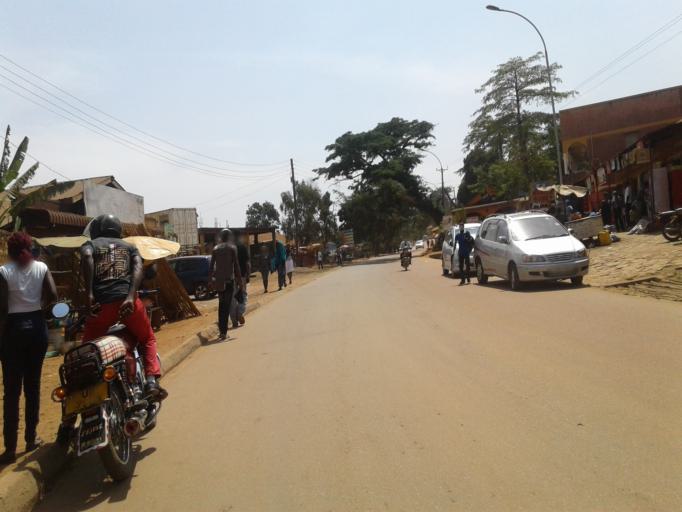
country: UG
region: Central Region
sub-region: Kampala District
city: Kampala
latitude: 0.2662
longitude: 32.6259
